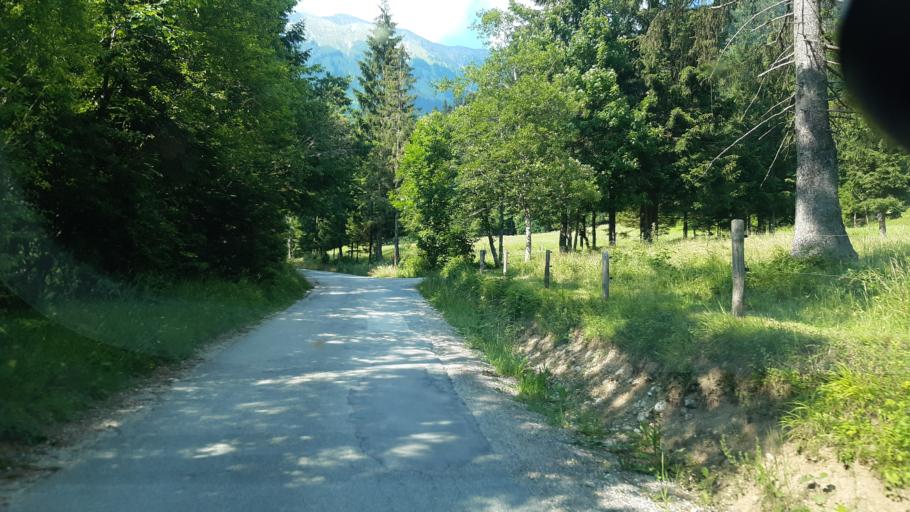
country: SI
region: Radovljica
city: Radovljica
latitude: 46.3906
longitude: 14.2176
